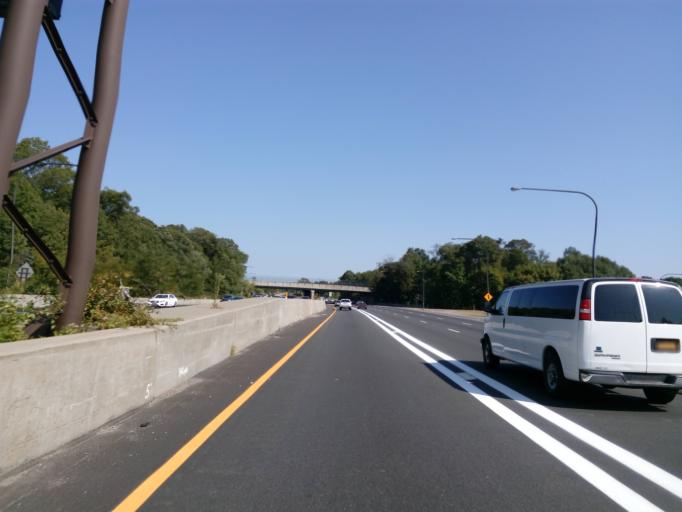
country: US
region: New York
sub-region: Nassau County
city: East Hills
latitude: 40.7837
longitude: -73.6258
